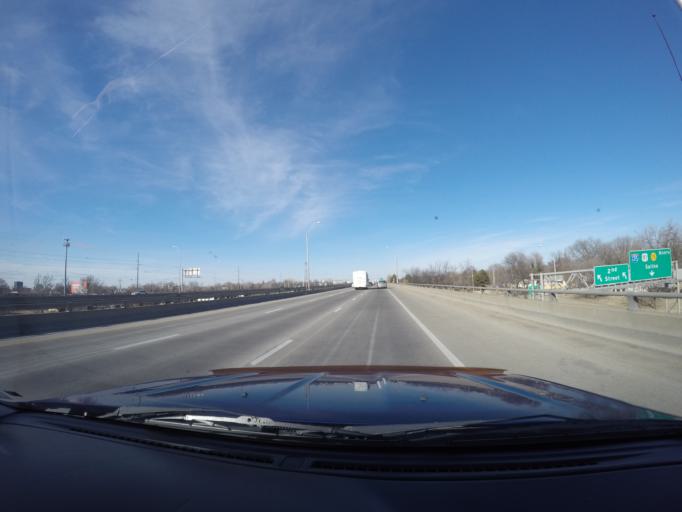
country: US
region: Kansas
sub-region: Sedgwick County
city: Wichita
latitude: 37.6889
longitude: -97.3136
